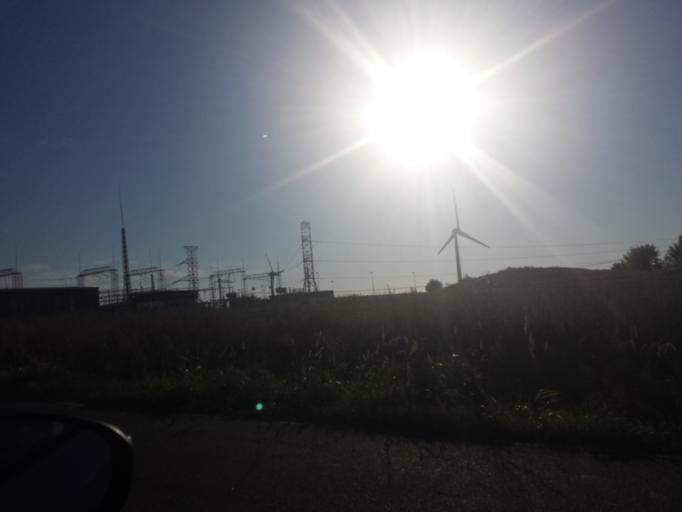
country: RO
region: Constanta
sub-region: Comuna Saraiu
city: Saraiu
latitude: 44.7958
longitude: 28.2408
